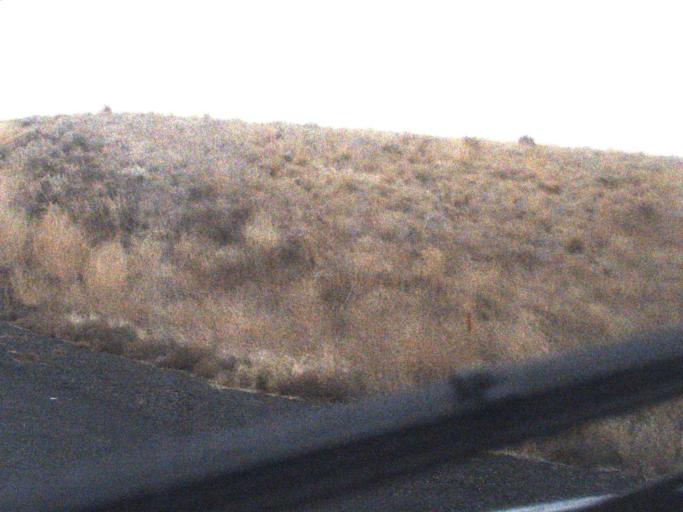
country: US
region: Washington
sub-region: Adams County
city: Ritzville
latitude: 46.7727
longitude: -118.3564
